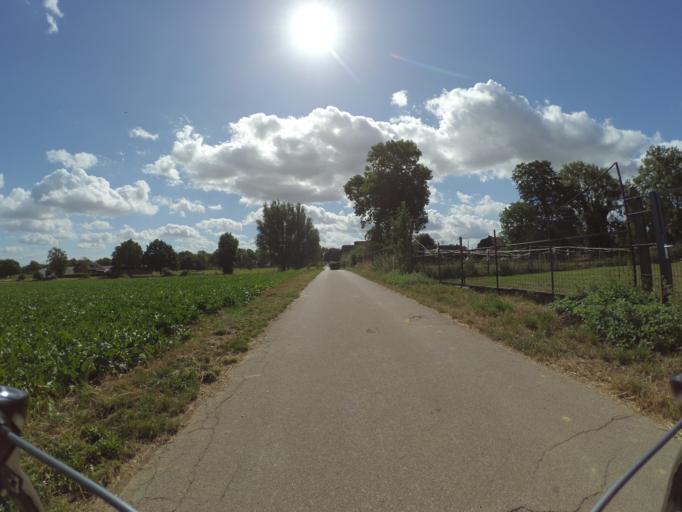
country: DE
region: North Rhine-Westphalia
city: Niedermerz
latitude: 50.8865
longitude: 6.2461
